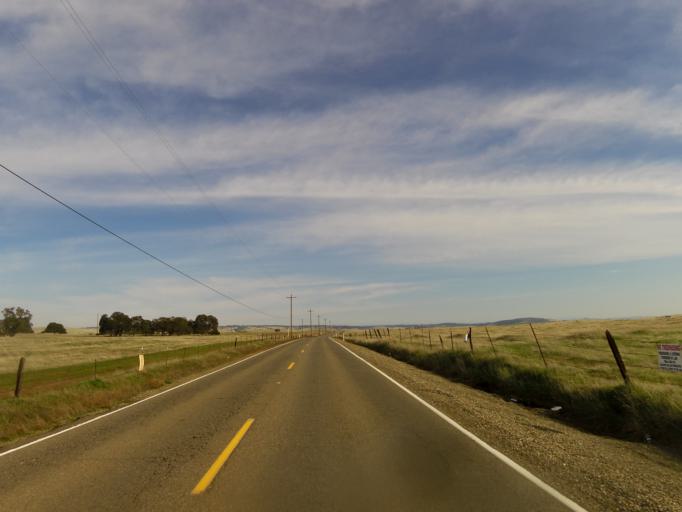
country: US
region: California
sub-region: Sacramento County
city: Folsom
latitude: 38.6179
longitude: -121.1370
